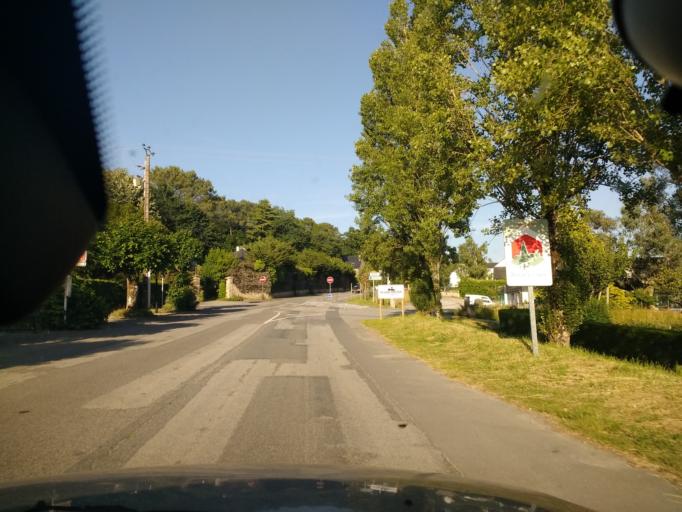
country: FR
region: Brittany
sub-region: Departement du Morbihan
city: Pluherlin
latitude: 47.6997
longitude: -2.3468
